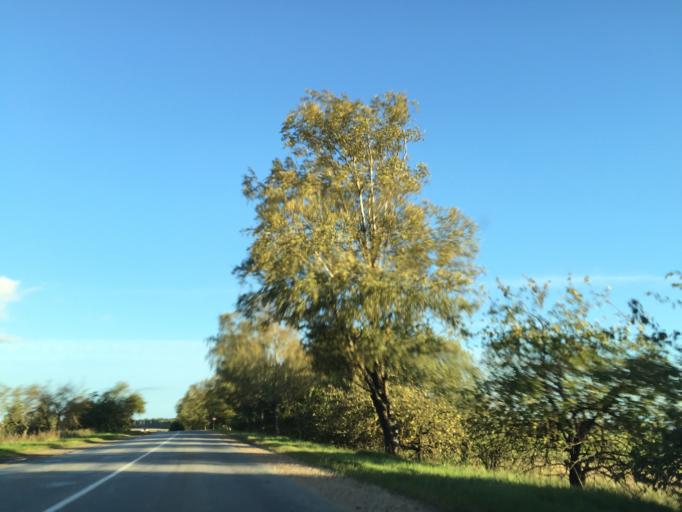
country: LV
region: Saldus Rajons
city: Saldus
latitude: 56.7198
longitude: 22.3880
